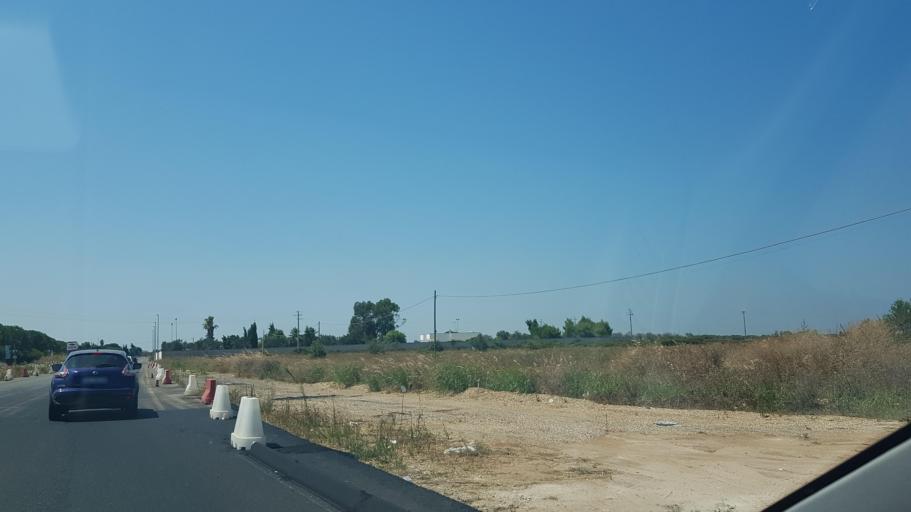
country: IT
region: Apulia
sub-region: Provincia di Lecce
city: Merine
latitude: 40.3354
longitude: 18.2353
